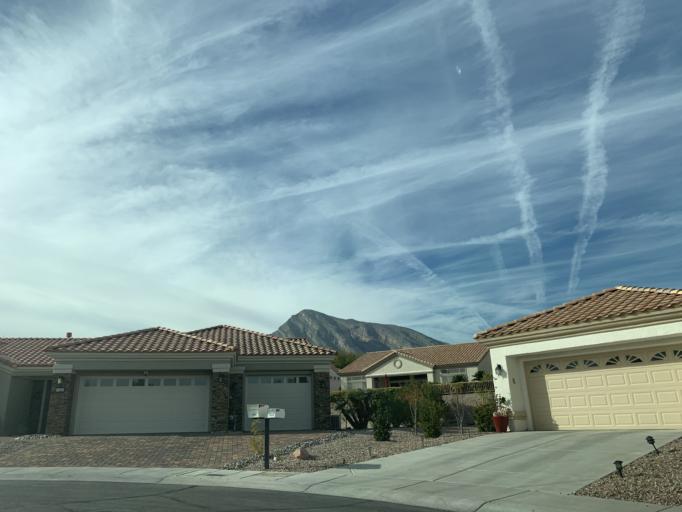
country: US
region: Nevada
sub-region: Clark County
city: Summerlin South
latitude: 36.2153
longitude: -115.3275
